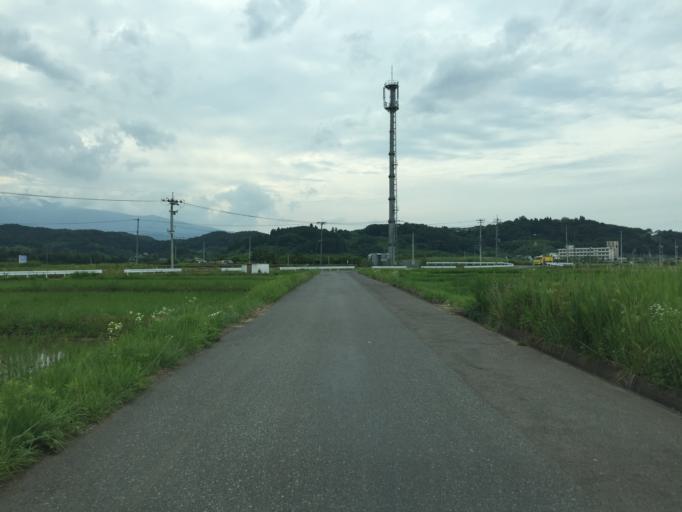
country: JP
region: Fukushima
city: Fukushima-shi
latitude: 37.7178
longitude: 140.4406
